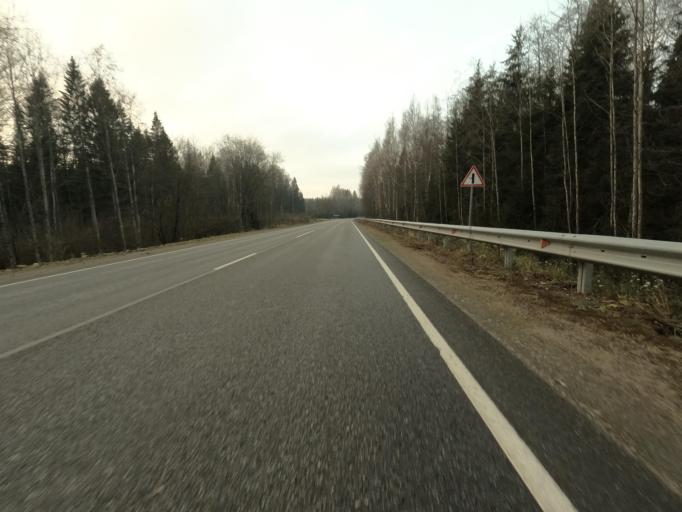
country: RU
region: Leningrad
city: Kirovsk
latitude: 59.8204
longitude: 30.9779
